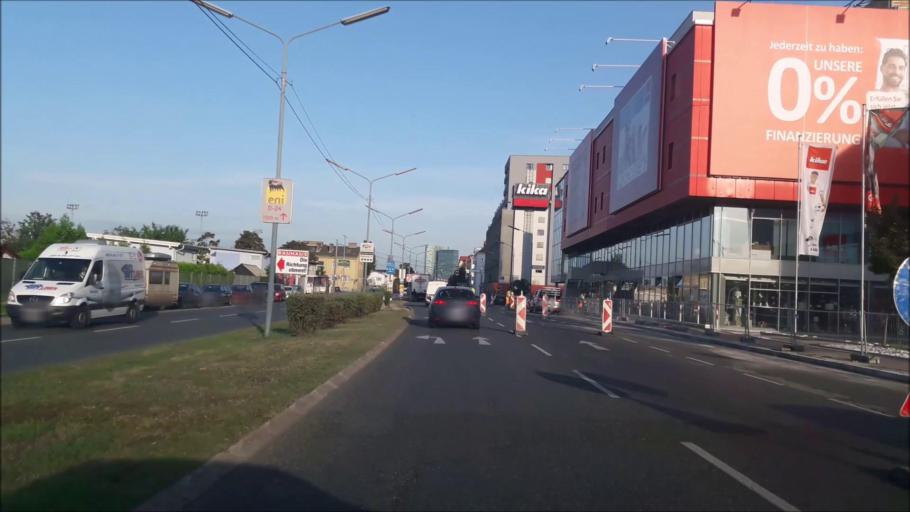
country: AT
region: Vienna
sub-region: Wien Stadt
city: Vienna
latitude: 48.1648
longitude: 16.3704
